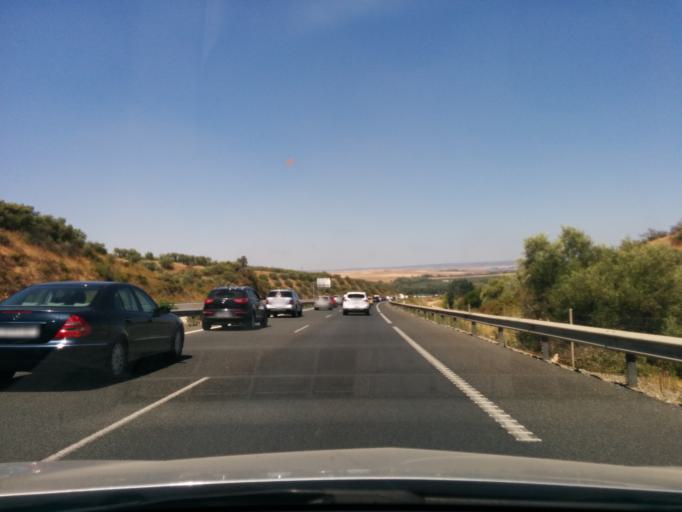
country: ES
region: Andalusia
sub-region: Provincia de Sevilla
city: Benacazon
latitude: 37.3645
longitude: -6.2112
